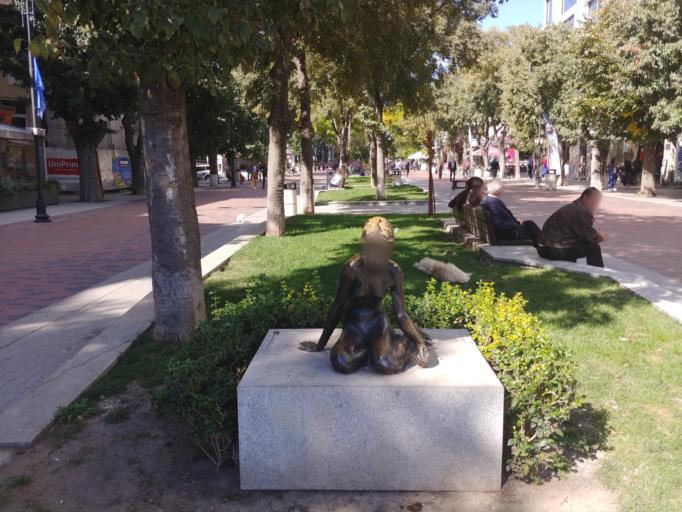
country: BG
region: Varna
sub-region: Obshtina Varna
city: Varna
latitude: 43.2045
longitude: 27.9212
